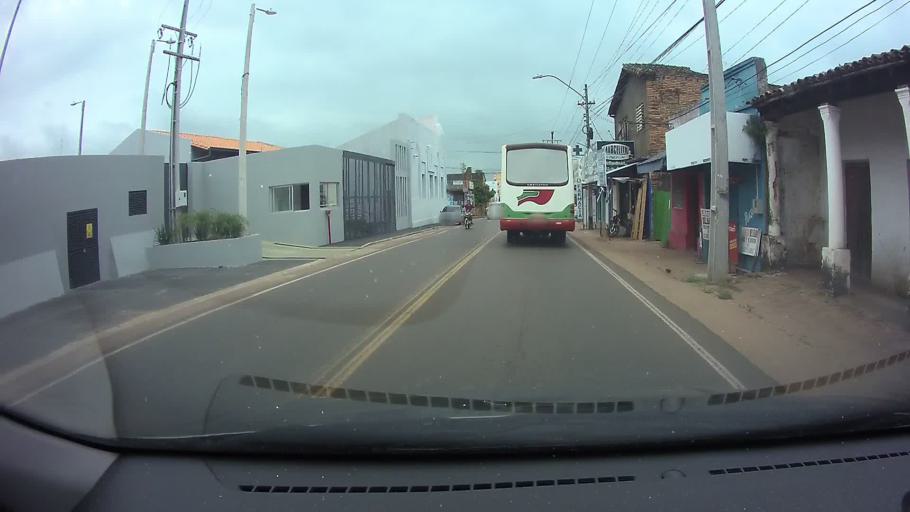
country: PY
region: Paraguari
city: Carapegua
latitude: -25.7688
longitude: -57.2427
